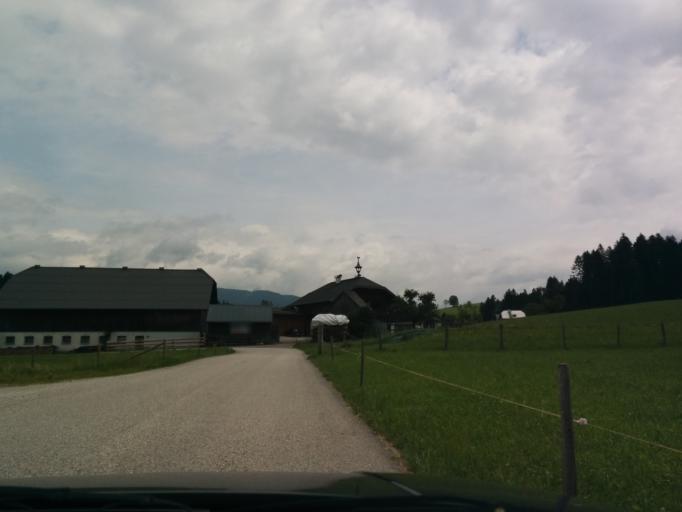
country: AT
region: Salzburg
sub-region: Politischer Bezirk Hallein
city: Abtenau
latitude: 47.5571
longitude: 13.3513
